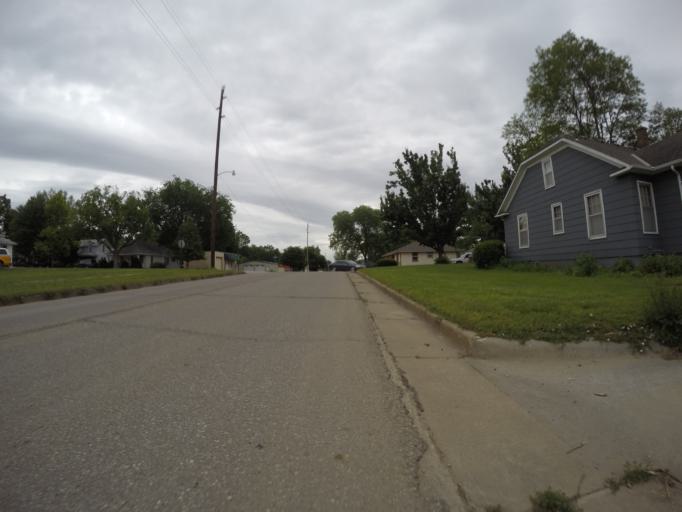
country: US
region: Kansas
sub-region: Pottawatomie County
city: Wamego
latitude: 39.2008
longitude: -96.3122
